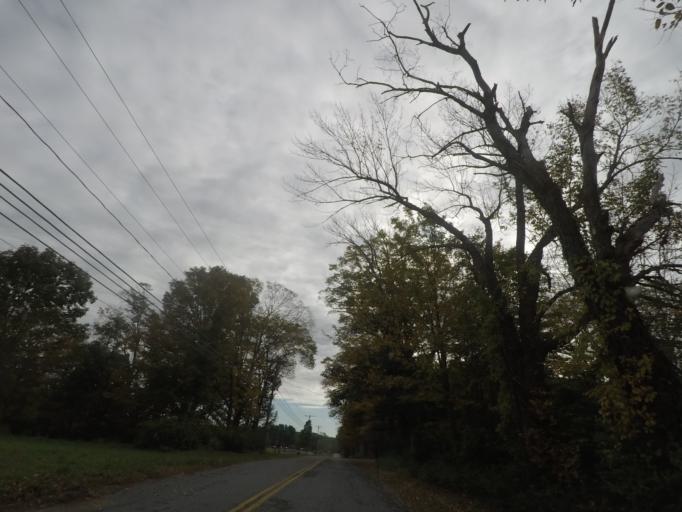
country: US
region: Connecticut
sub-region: Windham County
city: Thompson
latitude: 41.9520
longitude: -71.8470
